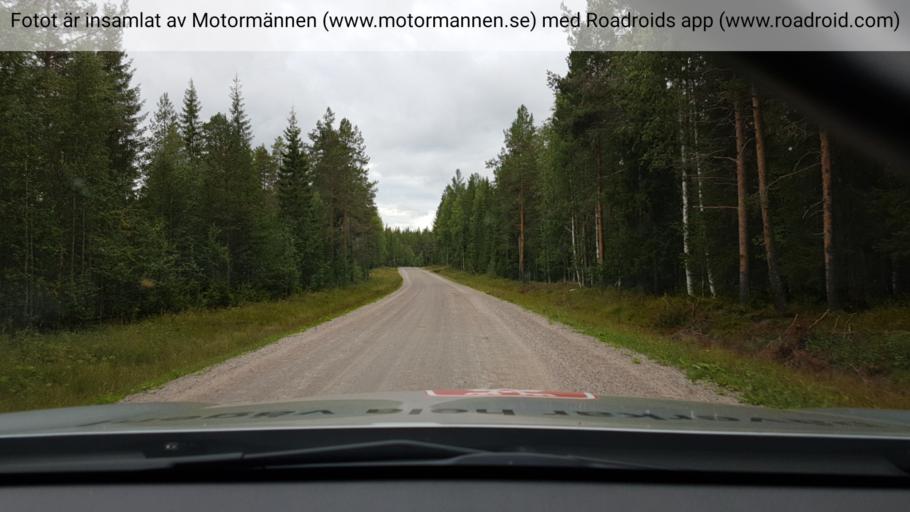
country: SE
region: Vaesterbotten
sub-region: Skelleftea Kommun
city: Forsbacka
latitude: 64.7501
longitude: 20.4171
